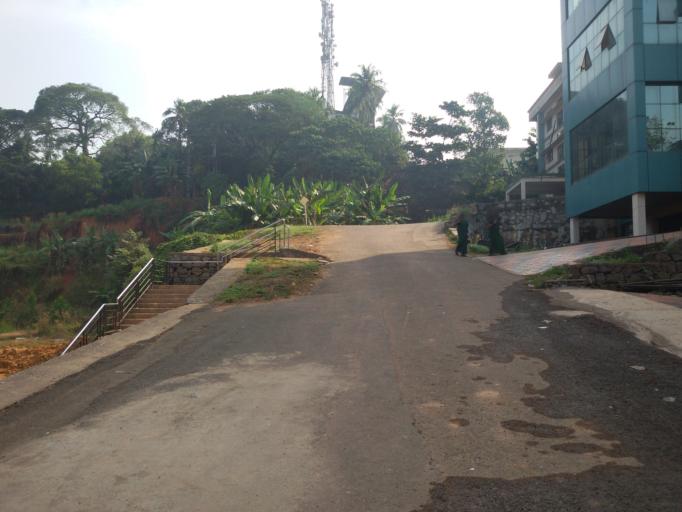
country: IN
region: Kerala
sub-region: Kozhikode
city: Kunnamangalam
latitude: 11.2941
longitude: 75.8225
